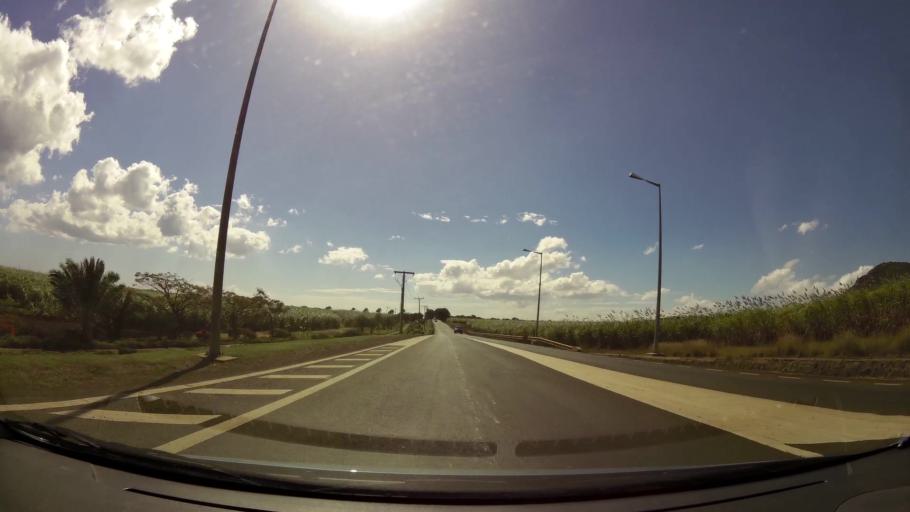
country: MU
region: Black River
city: Cascavelle
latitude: -20.2727
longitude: 57.4056
